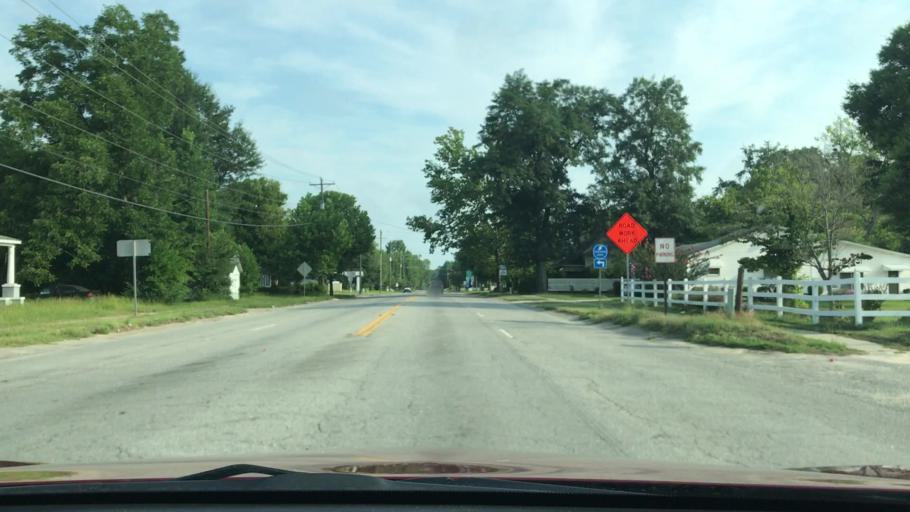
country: US
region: South Carolina
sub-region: Bamberg County
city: Denmark
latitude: 33.5321
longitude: -81.1232
